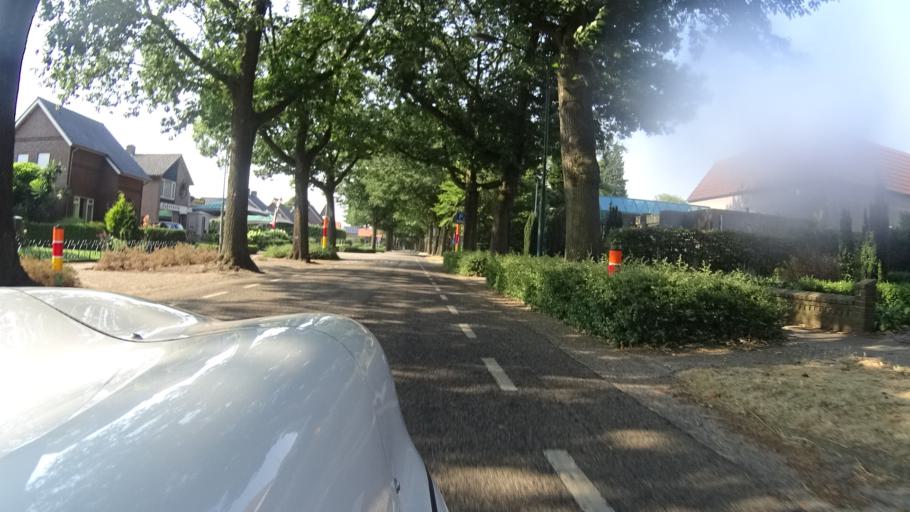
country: NL
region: North Brabant
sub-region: Gemeente Mill en Sint Hubert
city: Wilbertoord
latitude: 51.6541
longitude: 5.7740
